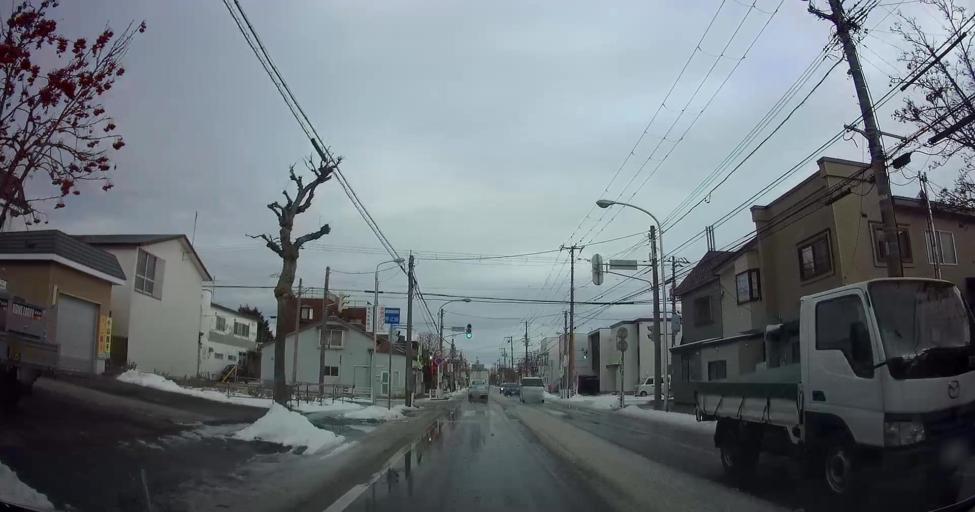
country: JP
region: Hokkaido
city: Hakodate
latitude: 41.7780
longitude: 140.7454
